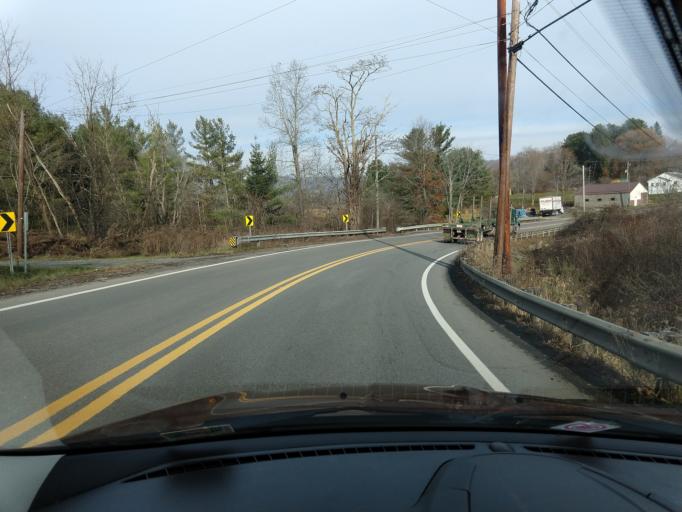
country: US
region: West Virginia
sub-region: Greenbrier County
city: Rainelle
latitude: 37.9437
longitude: -80.6523
